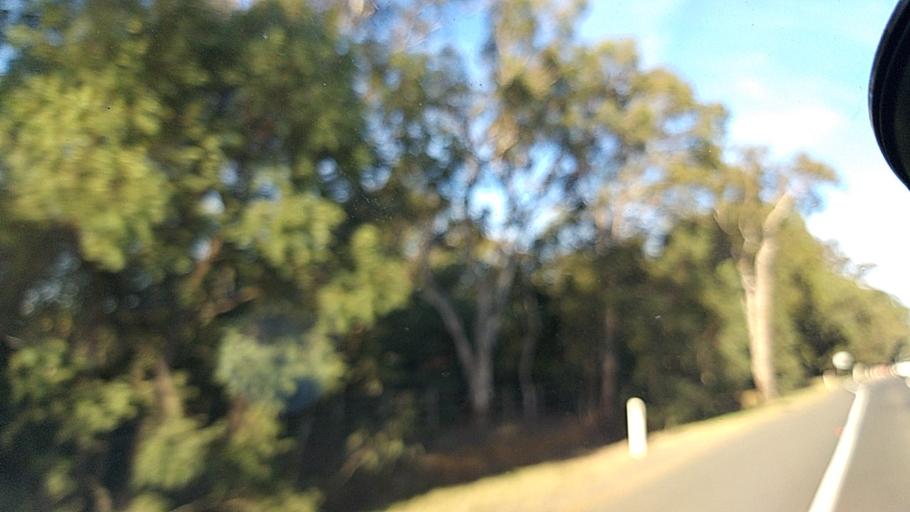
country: AU
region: New South Wales
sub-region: Hawkesbury
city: South Windsor
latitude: -33.6617
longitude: 150.7978
